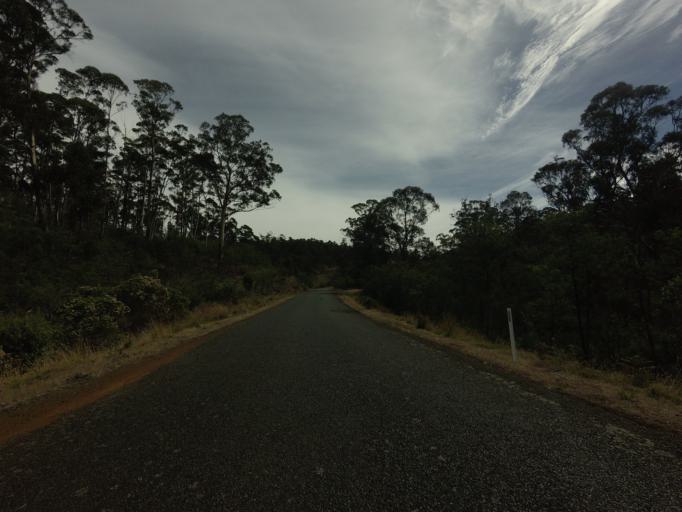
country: AU
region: Tasmania
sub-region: Sorell
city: Sorell
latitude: -42.5663
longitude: 147.6821
